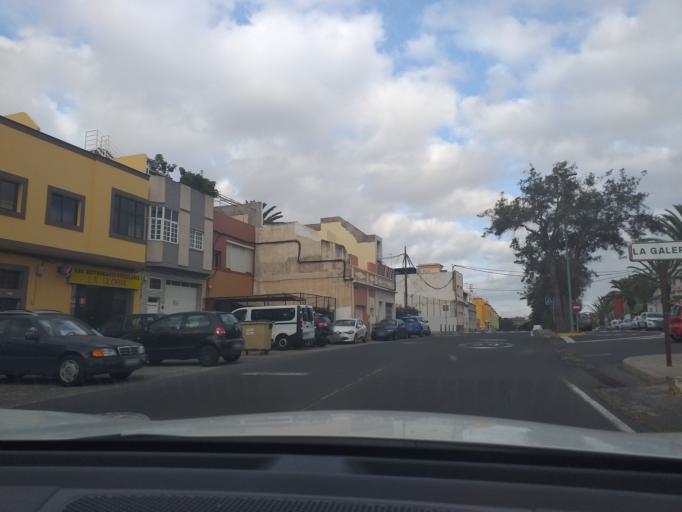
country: ES
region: Canary Islands
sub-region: Provincia de Las Palmas
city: Arucas
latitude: 28.0990
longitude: -15.4823
